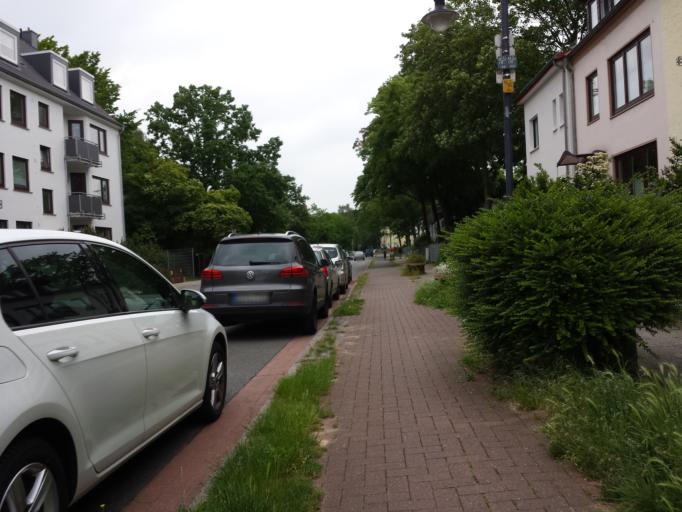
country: DE
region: Bremen
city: Bremen
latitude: 53.0990
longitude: 8.8041
